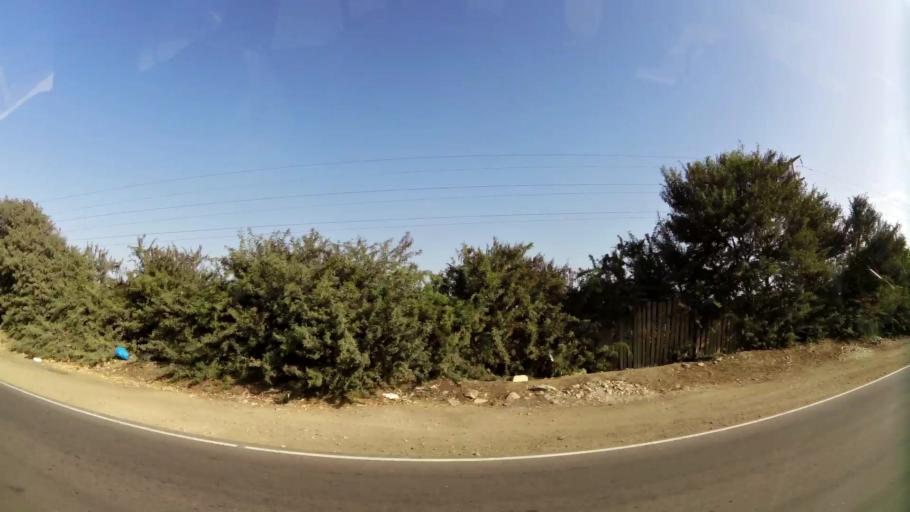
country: PE
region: Ica
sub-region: Provincia de Chincha
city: Chincha Baja
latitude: -13.4506
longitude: -76.1461
